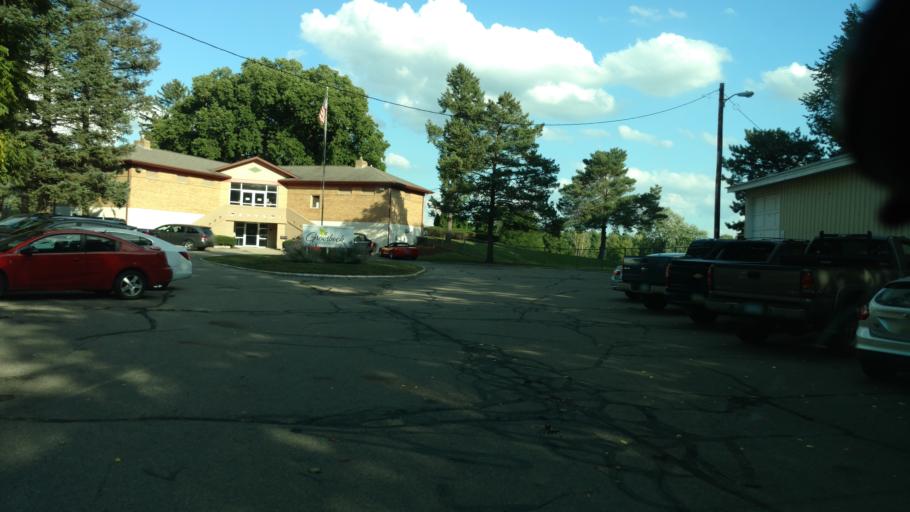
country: US
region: Michigan
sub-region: Ingham County
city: Lansing
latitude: 42.7477
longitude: -84.5272
